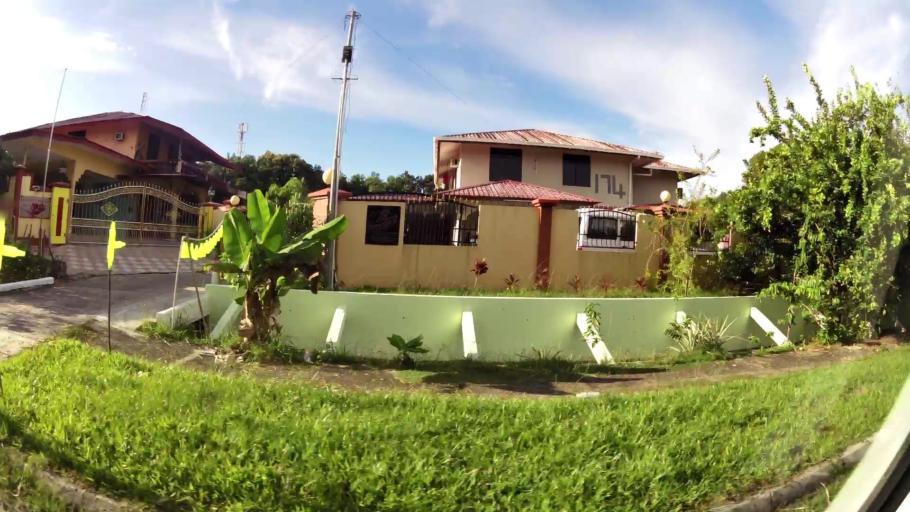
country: BN
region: Brunei and Muara
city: Bandar Seri Begawan
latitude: 4.9892
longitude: 114.9724
